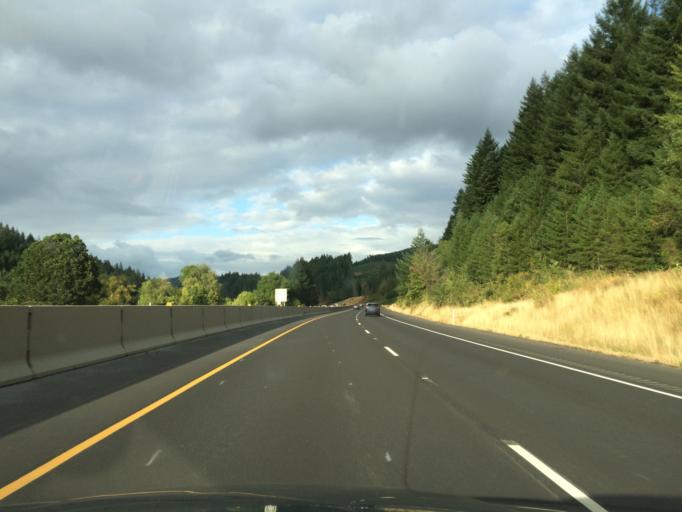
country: US
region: Oregon
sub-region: Douglas County
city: Drain
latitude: 43.7352
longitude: -123.1943
